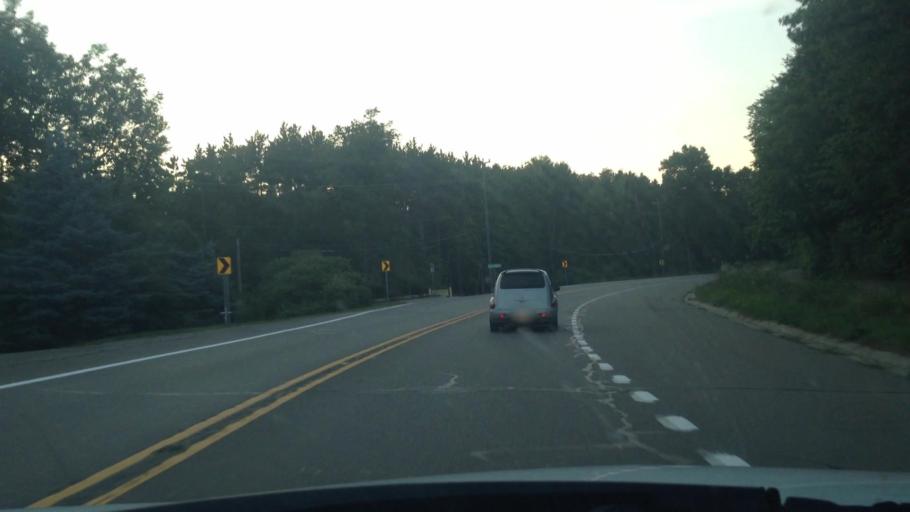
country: US
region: Michigan
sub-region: Oakland County
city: Lake Orion
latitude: 42.7583
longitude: -83.3134
